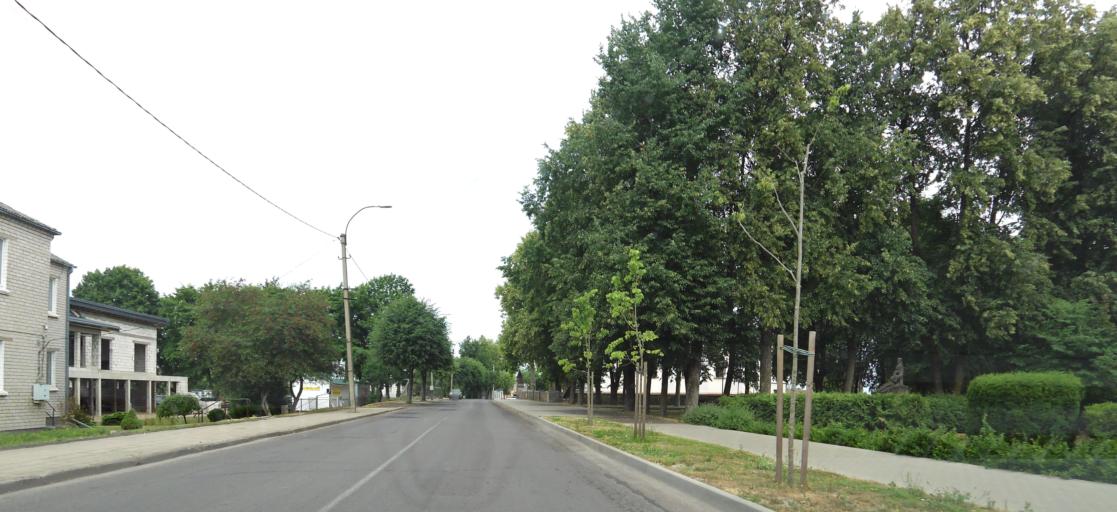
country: LT
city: Sirvintos
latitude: 55.0366
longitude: 24.9674
